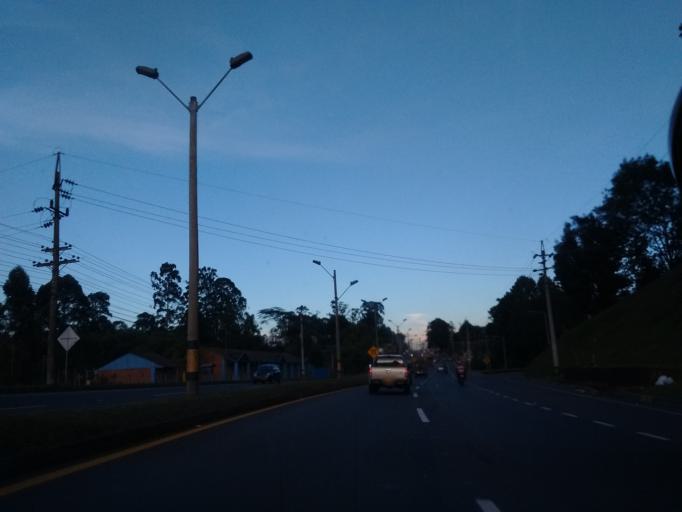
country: CO
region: Antioquia
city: Rionegro
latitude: 6.1794
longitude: -75.3630
